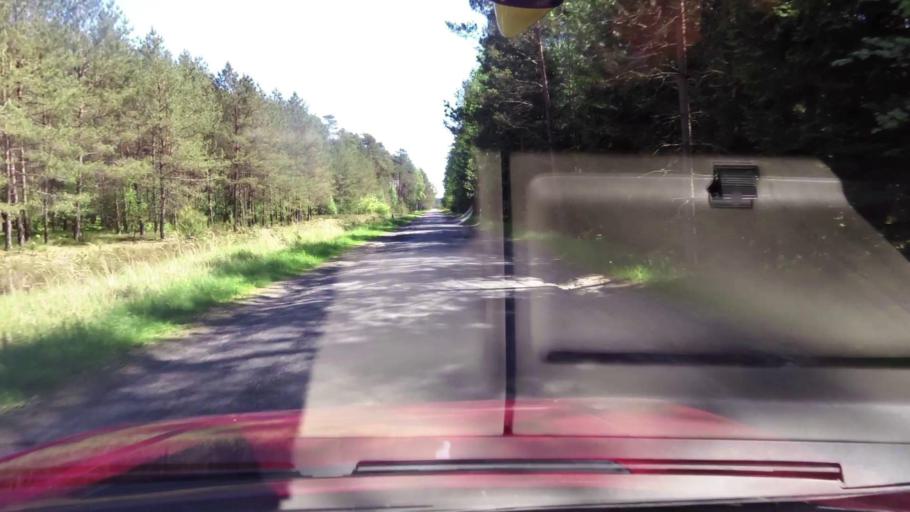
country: PL
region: West Pomeranian Voivodeship
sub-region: Powiat koszalinski
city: Sianow
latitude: 54.0784
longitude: 16.4209
